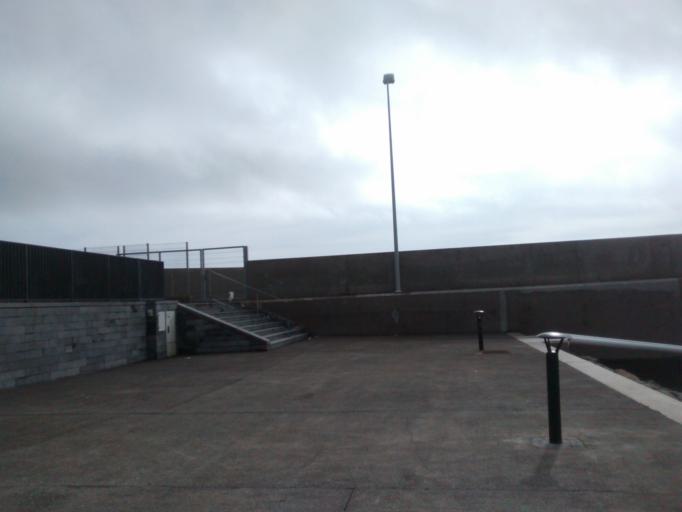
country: PT
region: Madeira
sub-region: Funchal
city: Funchal
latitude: 32.6457
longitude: -16.9067
